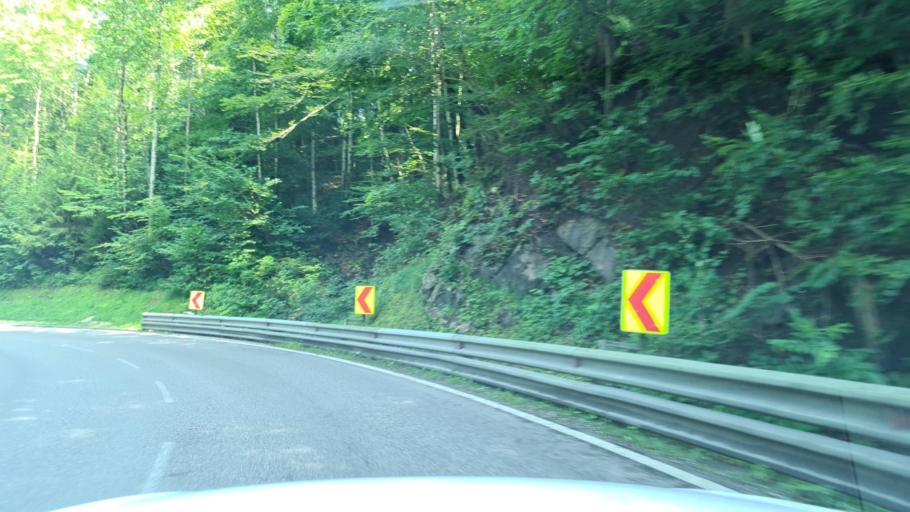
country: AT
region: Vorarlberg
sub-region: Politischer Bezirk Bregenz
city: Egg
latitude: 47.4534
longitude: 9.8705
